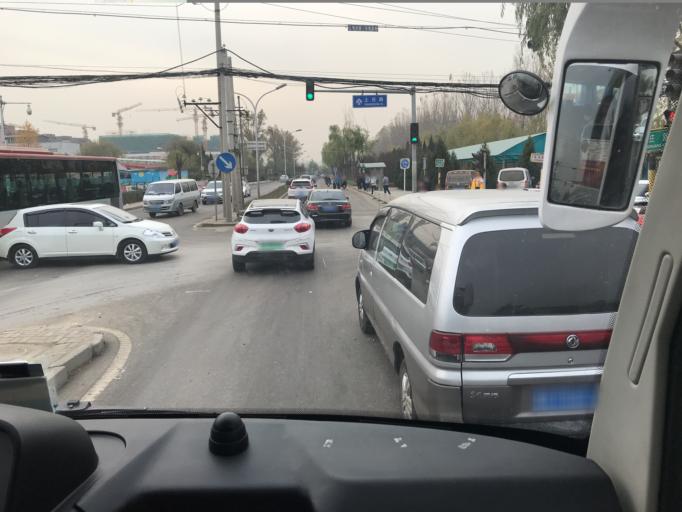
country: CN
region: Beijing
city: Sujiatuo
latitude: 40.0980
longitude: 116.2077
